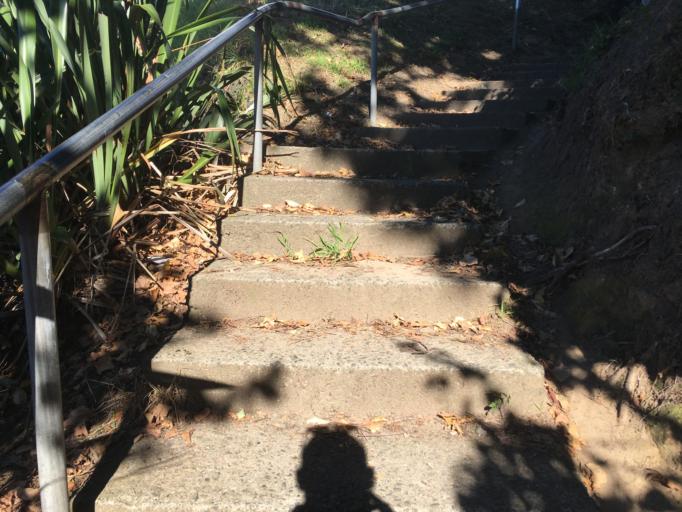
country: NZ
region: Bay of Plenty
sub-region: Tauranga City
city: Tauranga
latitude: -37.6875
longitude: 176.1698
